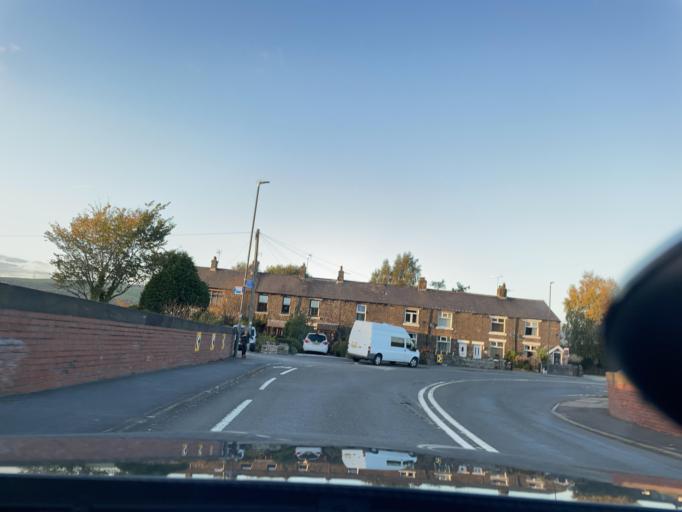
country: GB
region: England
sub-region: Borough of Tameside
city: Longdendale
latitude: 53.4430
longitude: -1.9878
